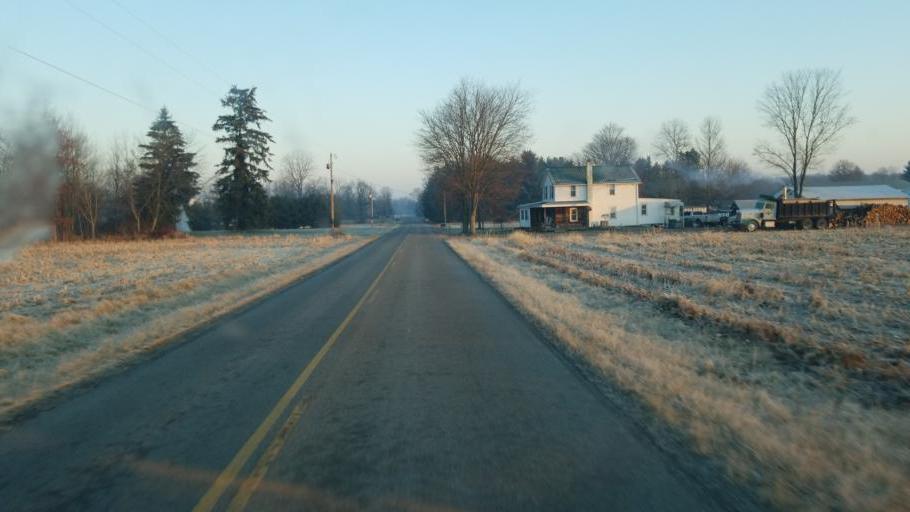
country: US
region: Ohio
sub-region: Medina County
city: Lodi
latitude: 40.9956
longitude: -82.0360
